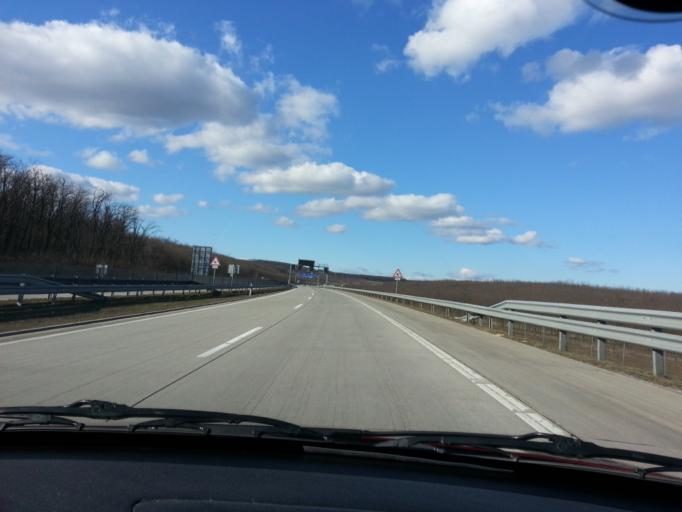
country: HU
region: Pest
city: Godollo
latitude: 47.5783
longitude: 19.3226
